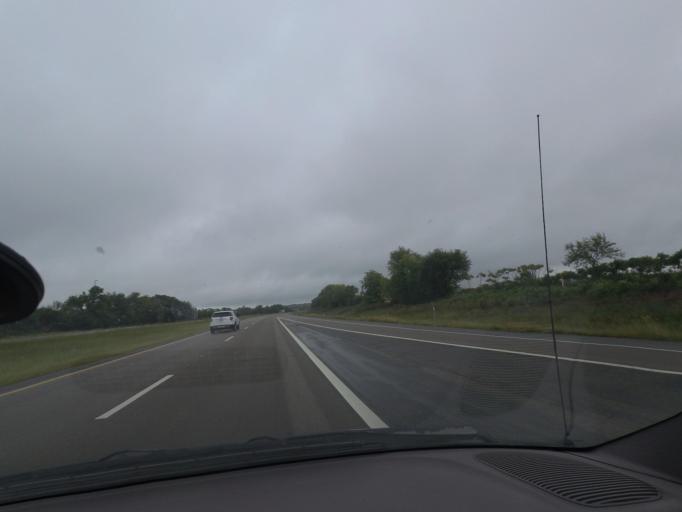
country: US
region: Illinois
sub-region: Piatt County
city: Monticello
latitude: 40.1077
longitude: -88.4893
